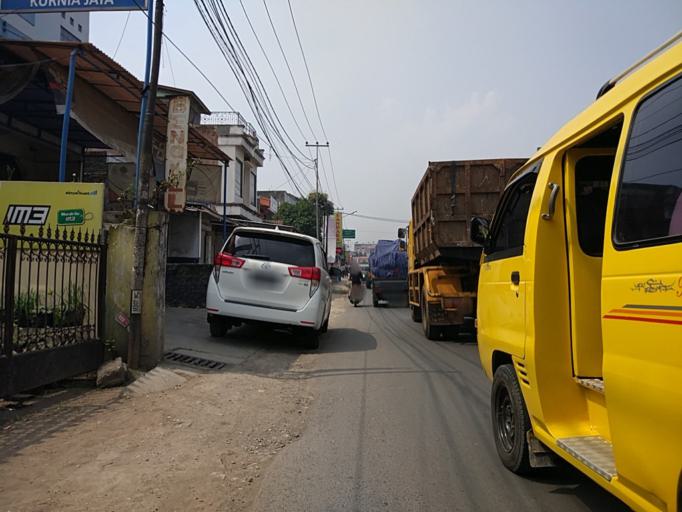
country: ID
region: West Java
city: Padalarang
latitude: -6.8416
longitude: 107.4822
